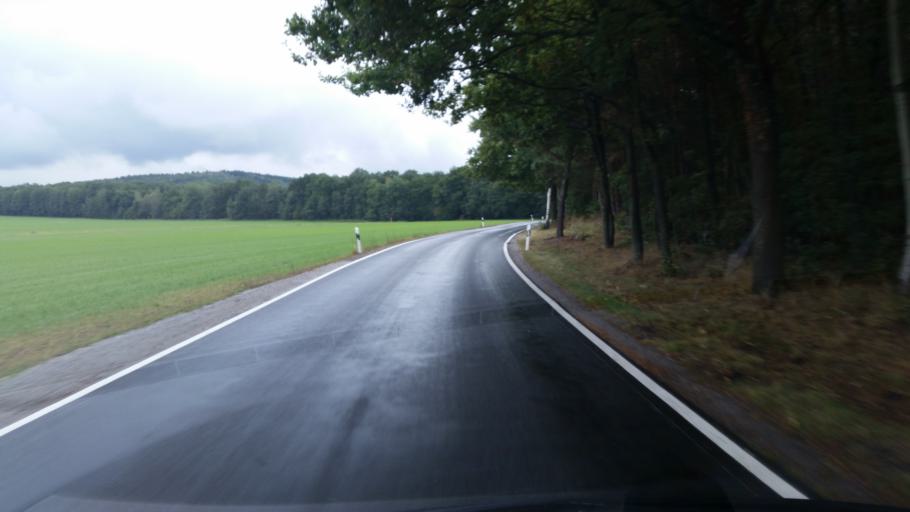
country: DE
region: Saxony
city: Kamenz
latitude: 51.2909
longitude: 14.0811
